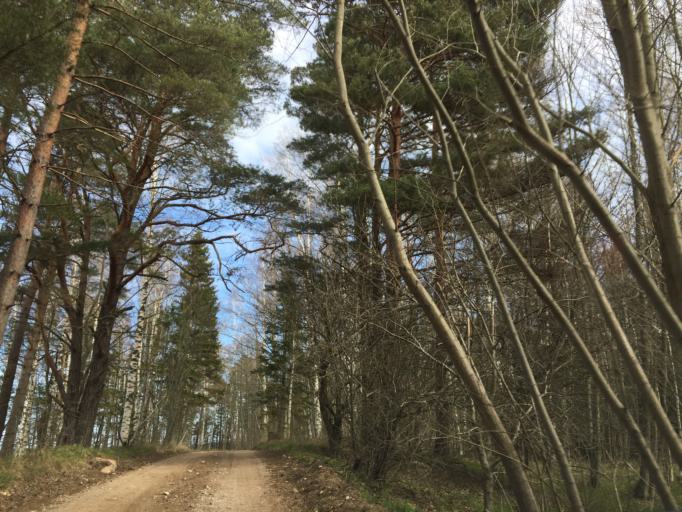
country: LV
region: Salacgrivas
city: Salacgriva
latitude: 57.6001
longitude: 24.3731
